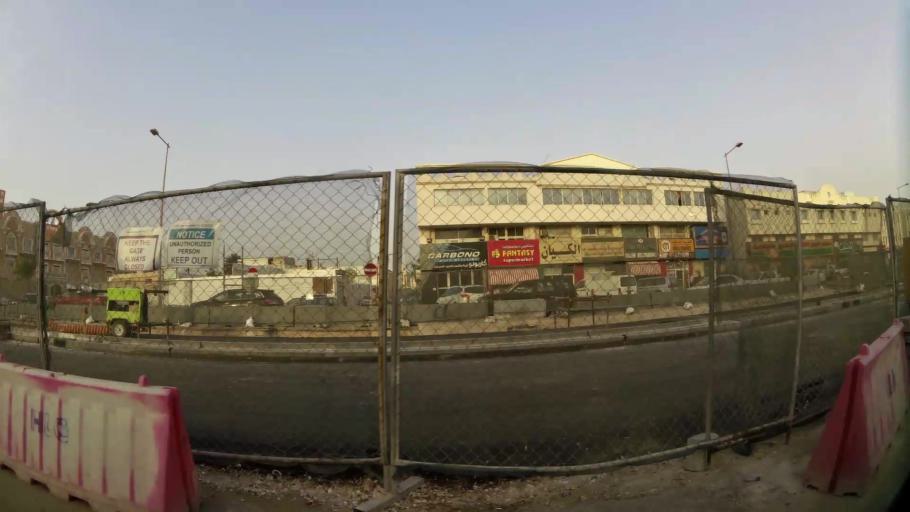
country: QA
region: Baladiyat ar Rayyan
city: Ar Rayyan
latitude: 25.2435
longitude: 51.4545
